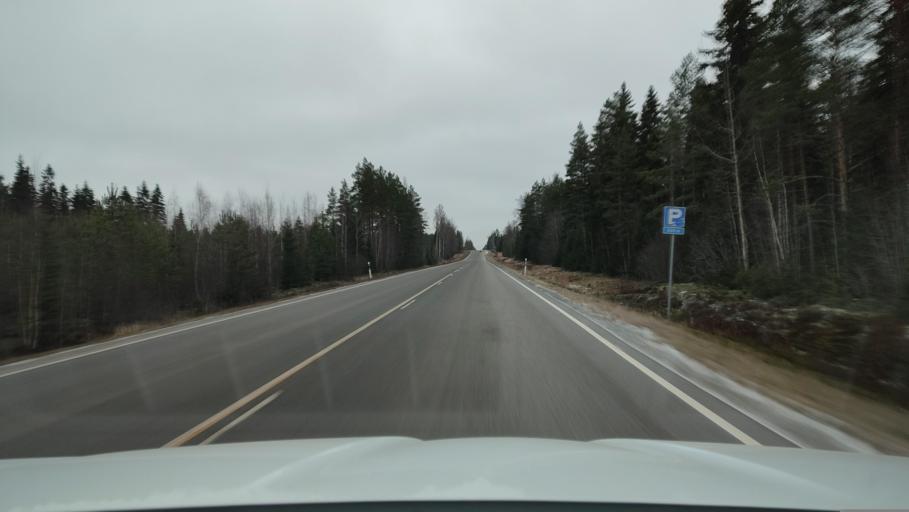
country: FI
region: Ostrobothnia
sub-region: Sydosterbotten
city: Naerpes
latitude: 62.4997
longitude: 21.4482
